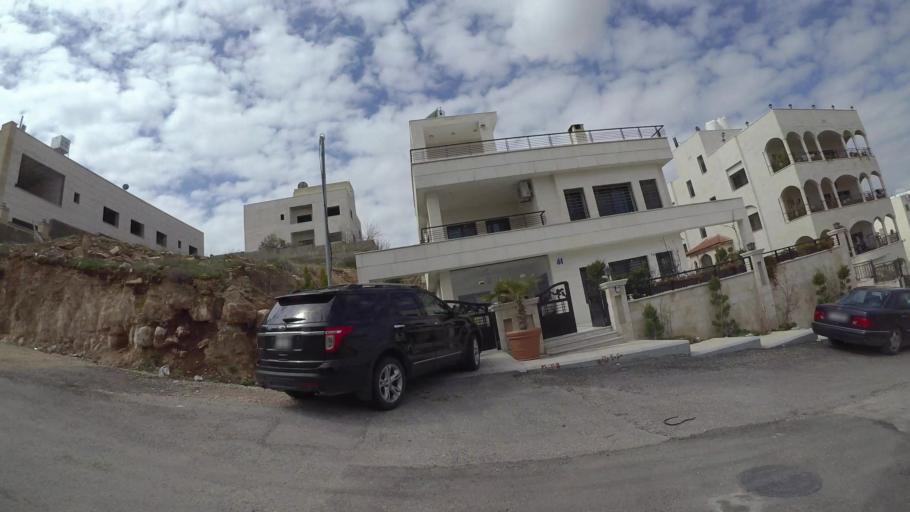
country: JO
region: Amman
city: Al Jubayhah
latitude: 32.0034
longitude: 35.9154
